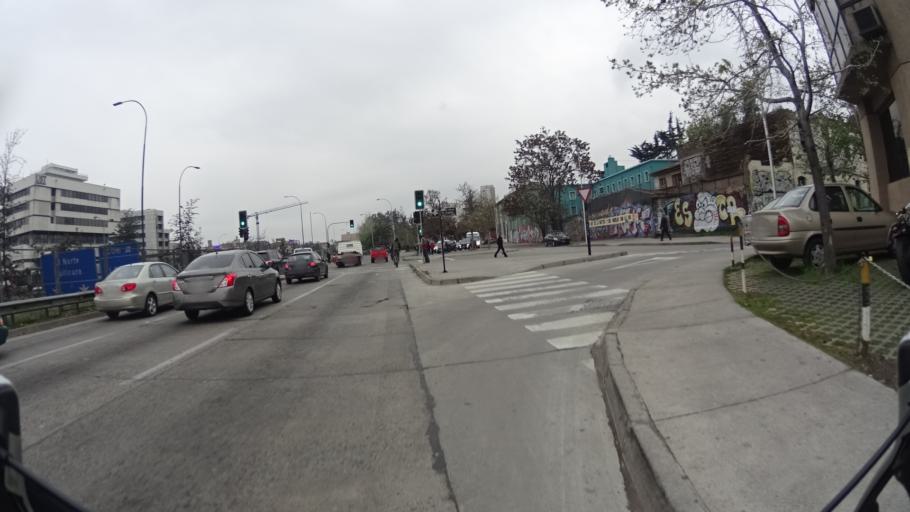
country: CL
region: Santiago Metropolitan
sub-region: Provincia de Santiago
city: Santiago
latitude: -33.4496
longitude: -70.6591
